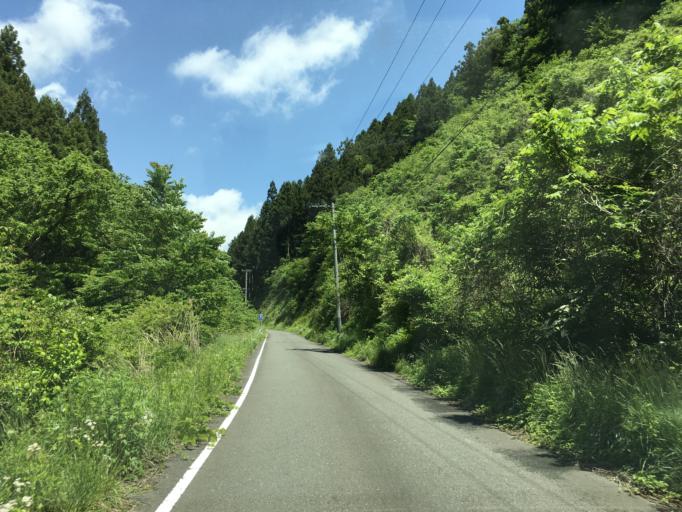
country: JP
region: Miyagi
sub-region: Oshika Gun
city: Onagawa Cho
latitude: 38.6762
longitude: 141.3475
